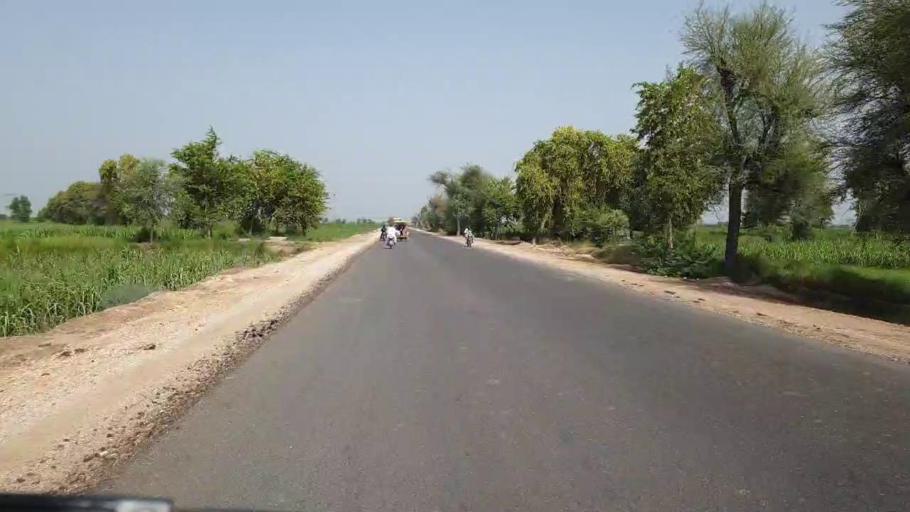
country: PK
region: Sindh
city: Sakrand
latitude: 26.2720
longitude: 68.1589
